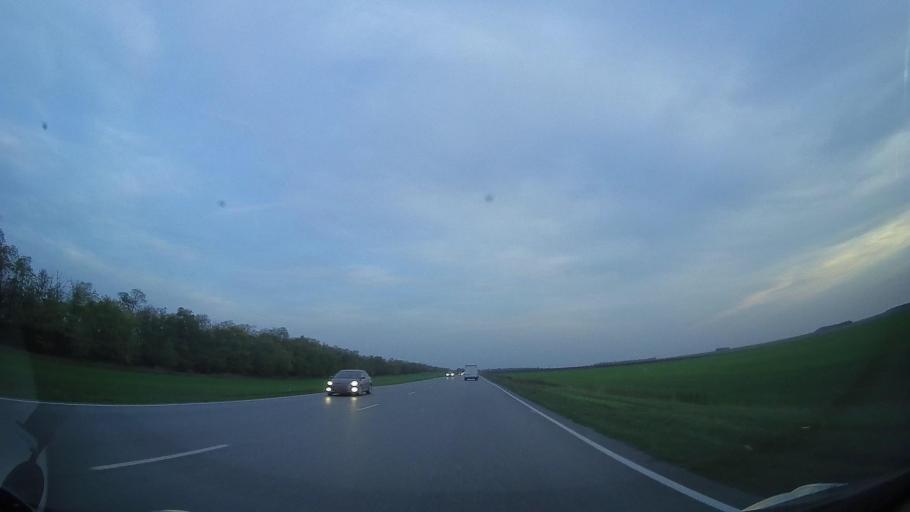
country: RU
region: Rostov
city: Kagal'nitskaya
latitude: 46.9067
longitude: 40.1174
